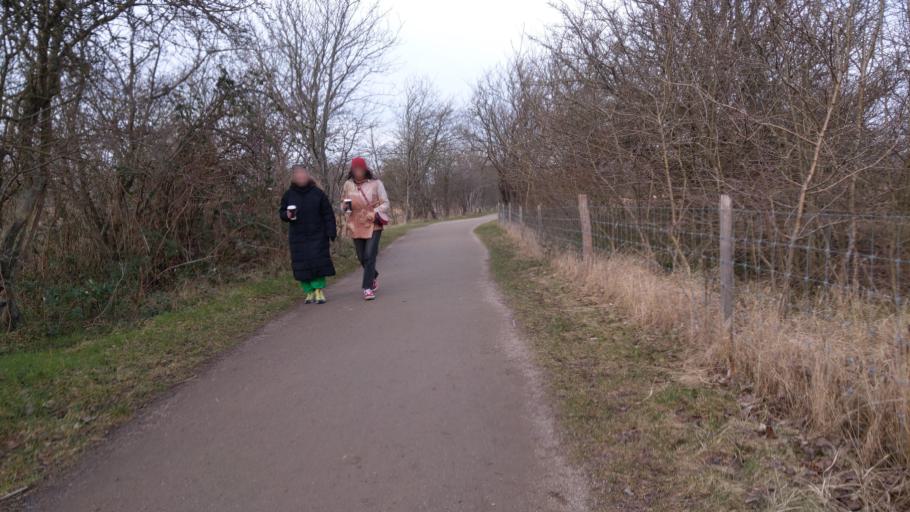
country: DK
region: Capital Region
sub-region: Frederiksberg Kommune
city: Frederiksberg
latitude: 55.6381
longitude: 12.5325
